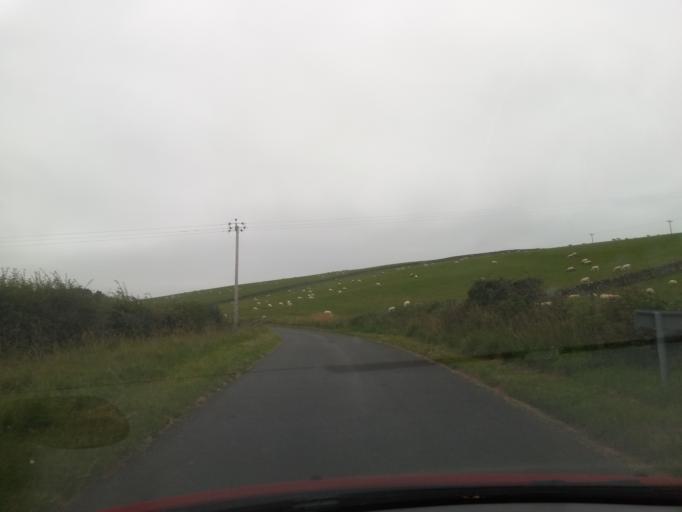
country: GB
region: Scotland
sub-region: Fife
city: Pathhead
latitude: 55.7318
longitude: -2.9060
